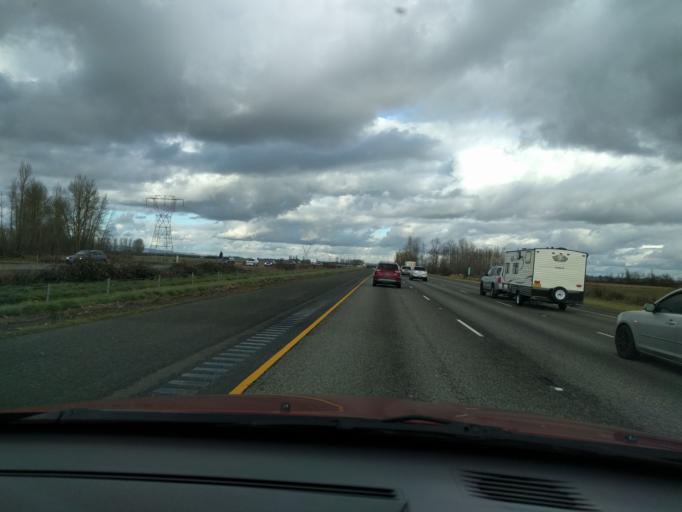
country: US
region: Oregon
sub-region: Marion County
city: Gervais
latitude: 45.1053
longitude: -122.9272
